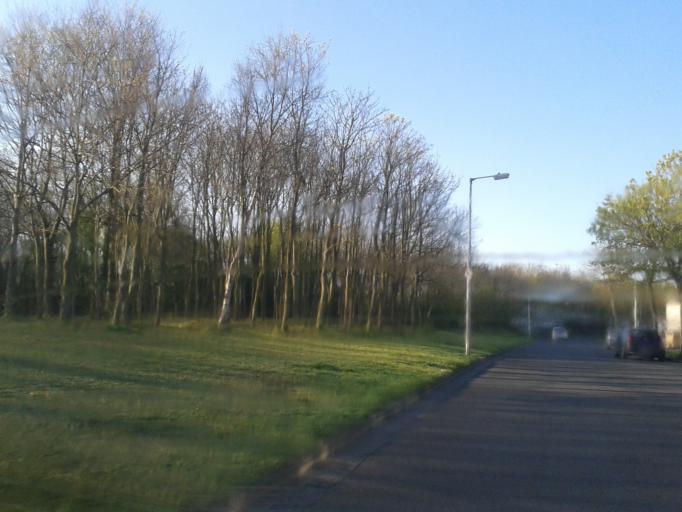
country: IE
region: Leinster
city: Beaumont
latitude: 53.4015
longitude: -6.2363
